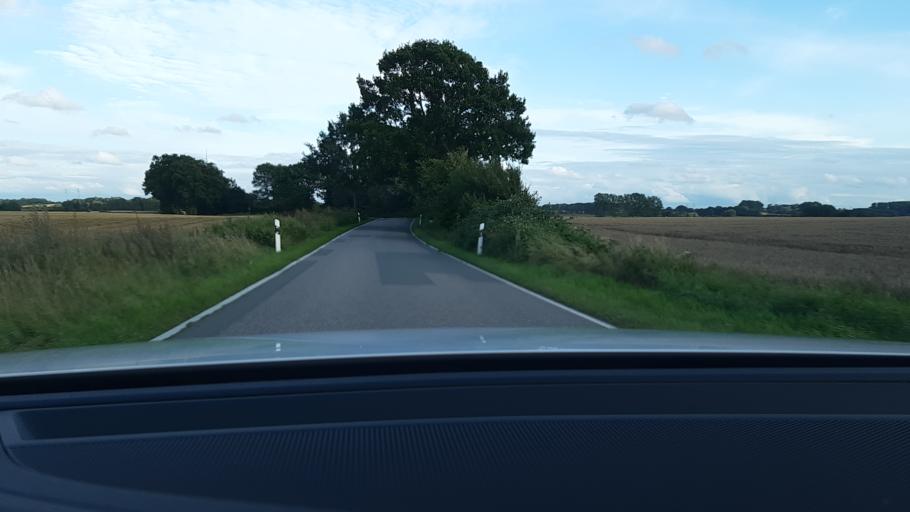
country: DE
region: Schleswig-Holstein
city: Stockelsdorf
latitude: 53.9201
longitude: 10.6193
